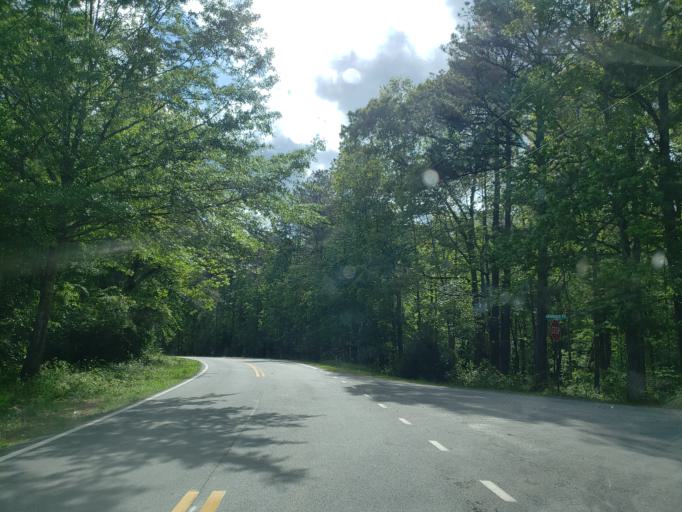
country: US
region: Georgia
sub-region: Carroll County
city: Mount Zion
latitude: 33.6806
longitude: -85.2163
